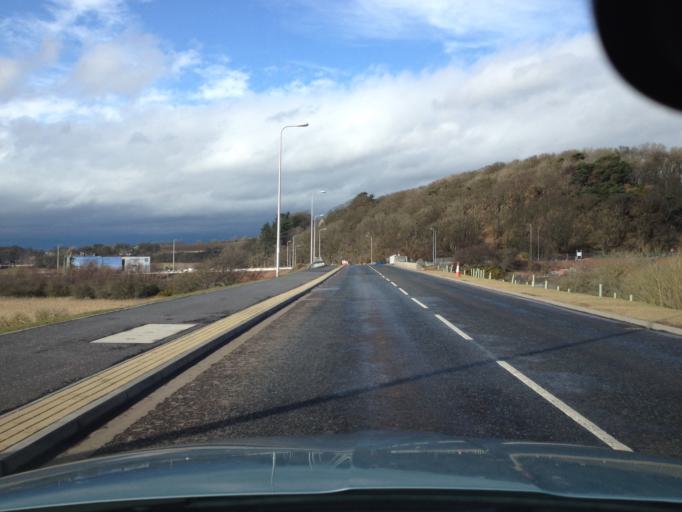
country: GB
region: Scotland
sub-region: Fife
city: Inverkeithing
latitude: 56.0193
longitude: -3.4121
